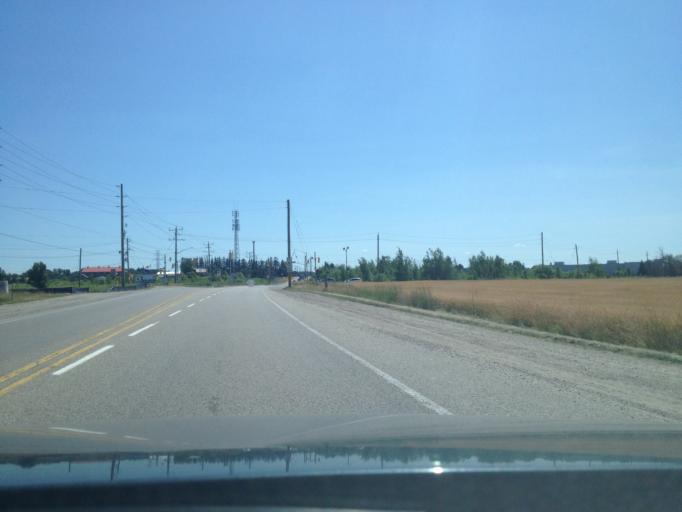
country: CA
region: Ontario
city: Waterloo
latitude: 43.5193
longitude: -80.5166
